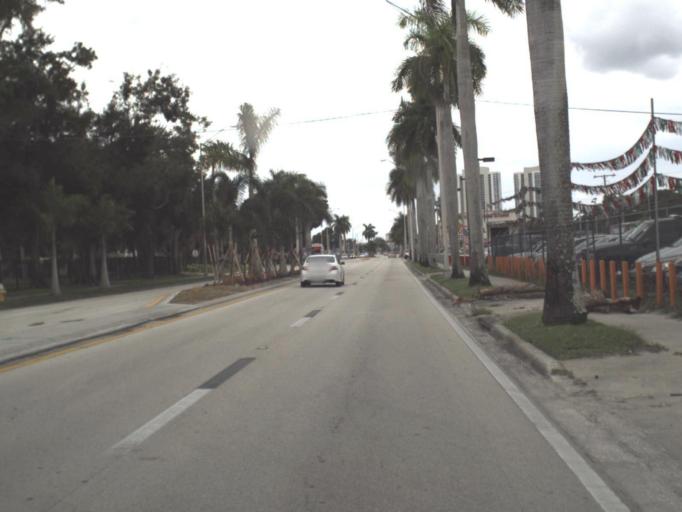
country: US
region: Florida
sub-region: Lee County
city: Tice
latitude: 26.6596
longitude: -81.8426
